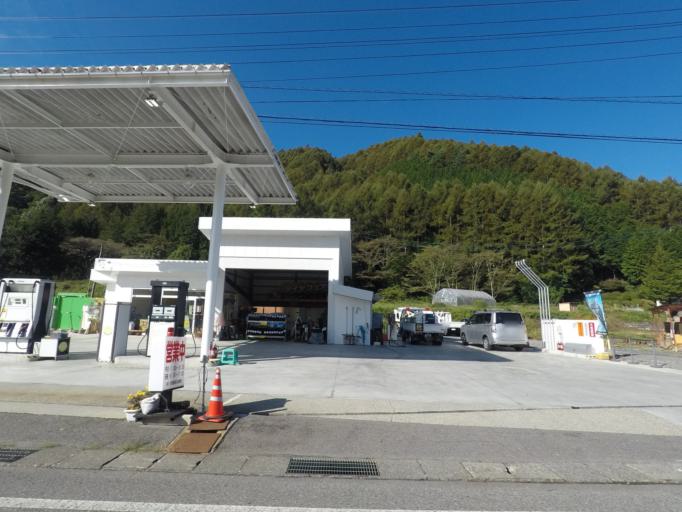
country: JP
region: Nagano
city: Ina
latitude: 35.9551
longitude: 137.7705
